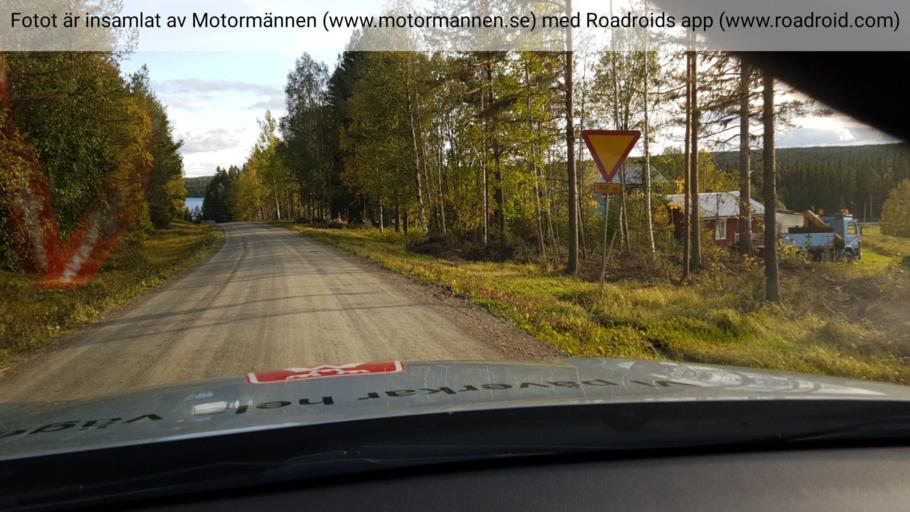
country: SE
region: Jaemtland
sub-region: Krokoms Kommun
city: Krokom
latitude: 63.6791
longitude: 14.5781
